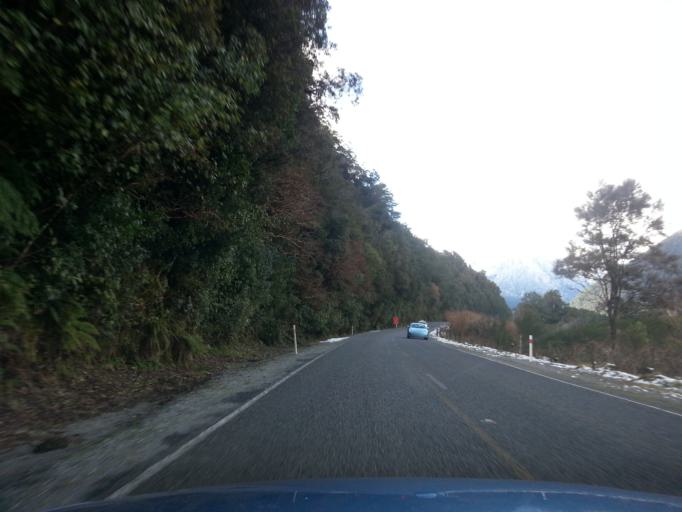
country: NZ
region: West Coast
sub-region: Grey District
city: Greymouth
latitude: -42.7849
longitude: 171.6057
